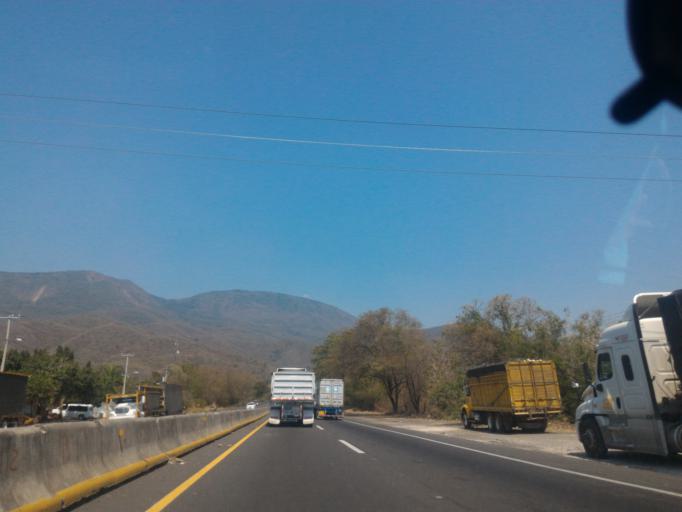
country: MX
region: Colima
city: Madrid
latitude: 19.0131
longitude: -103.8310
